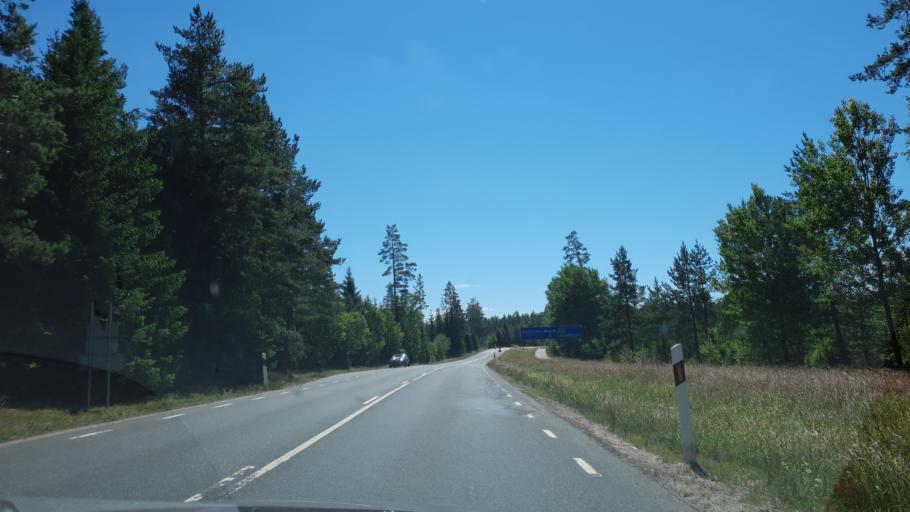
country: SE
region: Joenkoeping
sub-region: Vaggeryds Kommun
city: Vaggeryd
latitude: 57.5260
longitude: 14.1378
